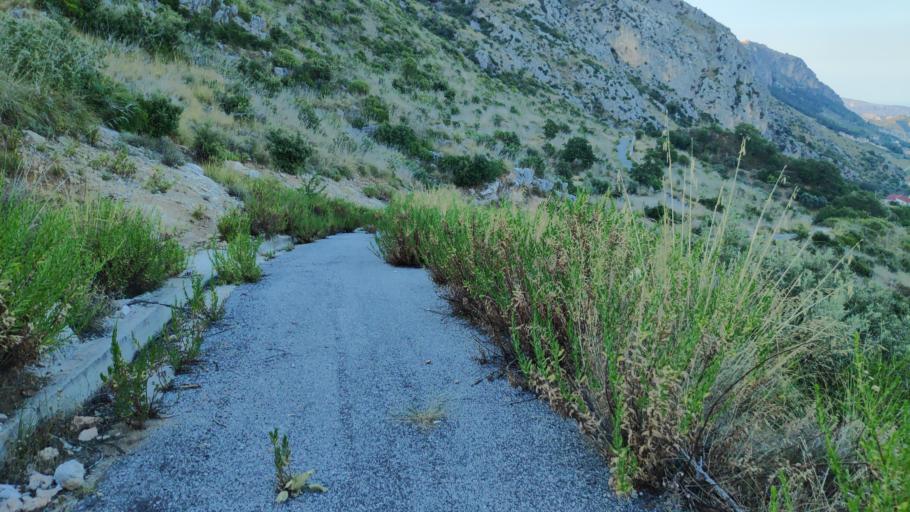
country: IT
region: Calabria
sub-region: Provincia di Reggio Calabria
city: Pazzano
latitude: 38.4624
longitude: 16.4469
